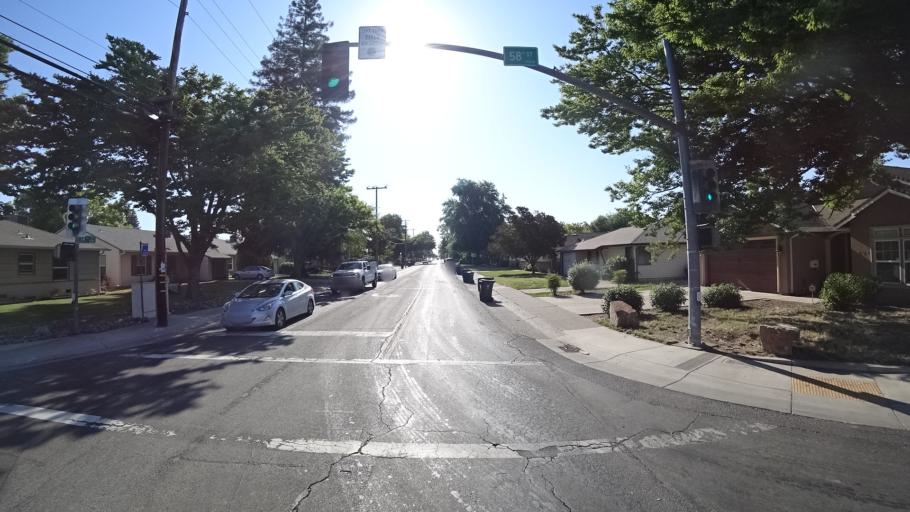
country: US
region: California
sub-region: Sacramento County
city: Parkway
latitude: 38.5395
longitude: -121.4385
